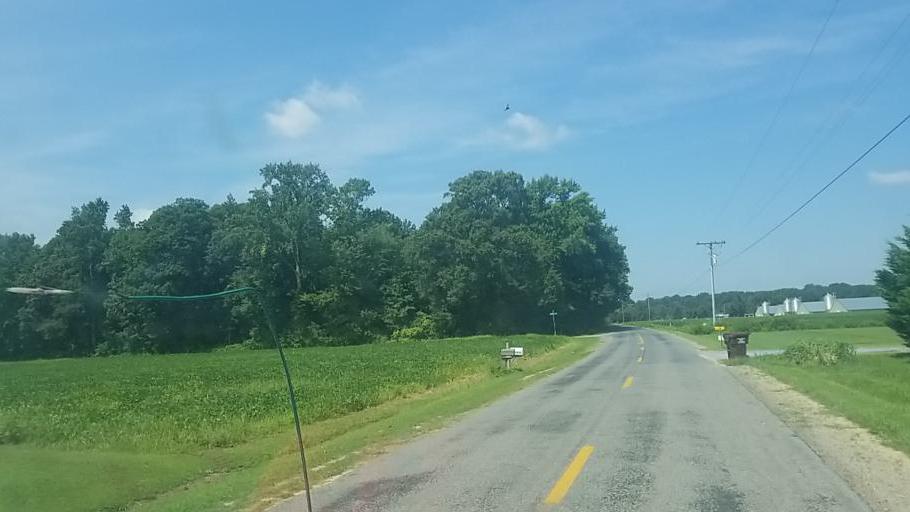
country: US
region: Maryland
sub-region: Caroline County
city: Denton
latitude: 38.8772
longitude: -75.7683
